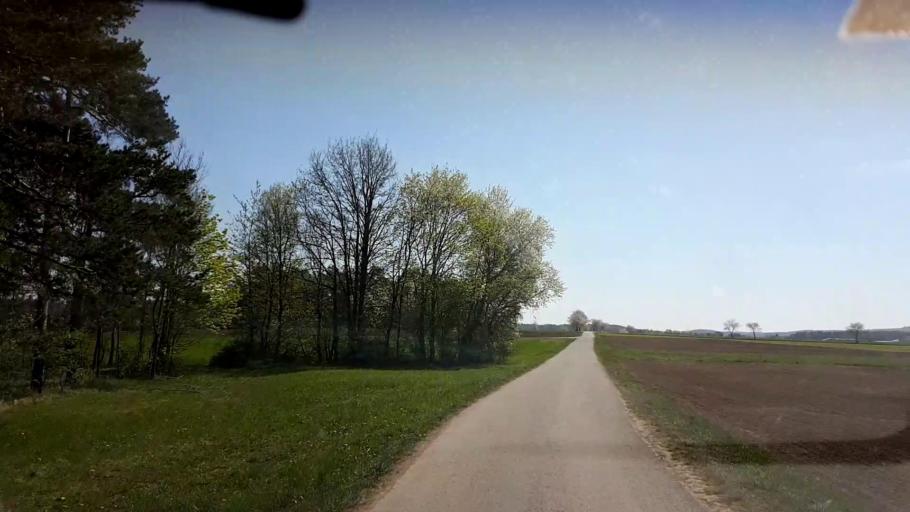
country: DE
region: Bavaria
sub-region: Upper Franconia
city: Heiligenstadt
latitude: 49.9042
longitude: 11.1751
